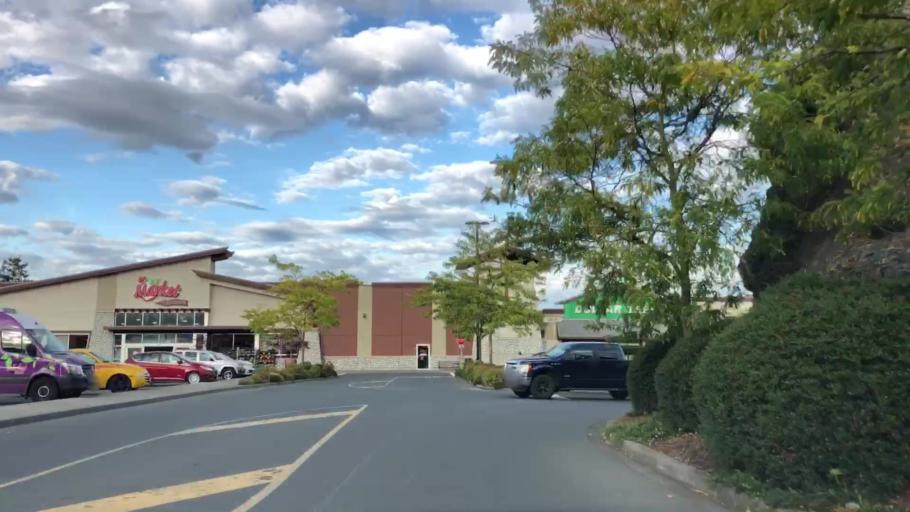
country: CA
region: British Columbia
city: Langford
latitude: 48.4620
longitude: -123.4969
